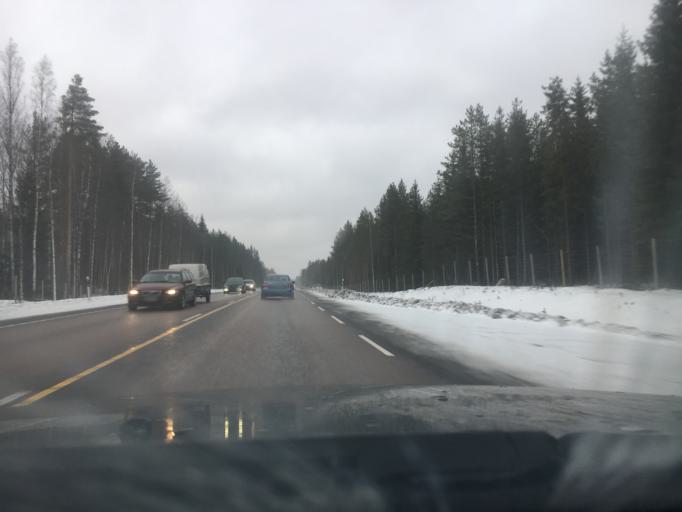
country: FI
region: Central Finland
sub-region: Joutsa
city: Leivonmaeki
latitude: 61.8336
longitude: 26.0965
